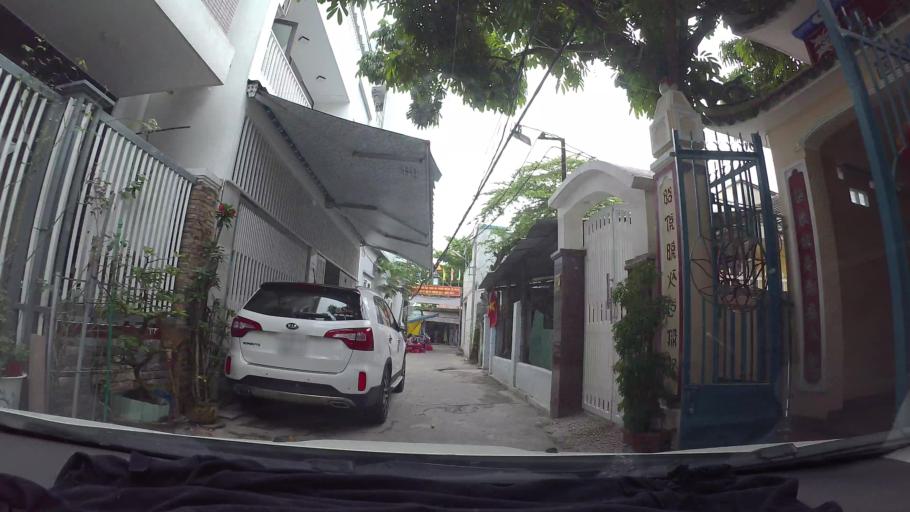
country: VN
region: Da Nang
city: Thanh Khe
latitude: 16.0646
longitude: 108.1891
